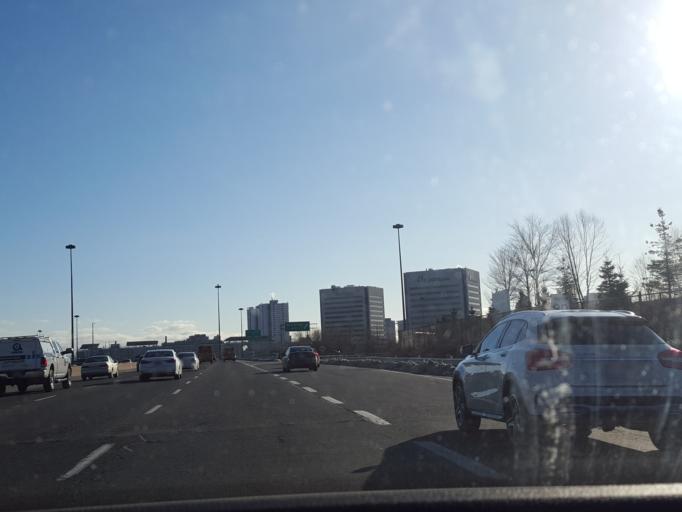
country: CA
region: Ontario
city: Willowdale
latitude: 43.7263
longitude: -79.3306
